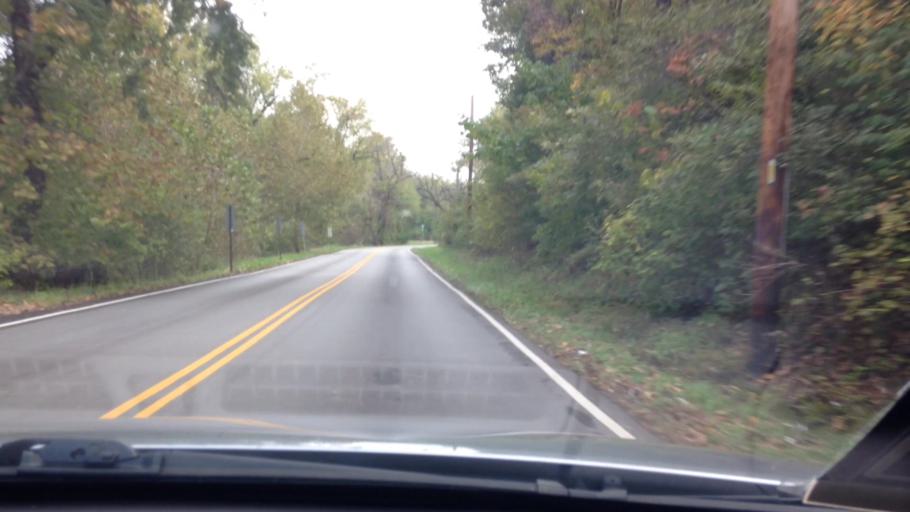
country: US
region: Kansas
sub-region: Leavenworth County
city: Lansing
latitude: 39.2445
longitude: -94.8015
